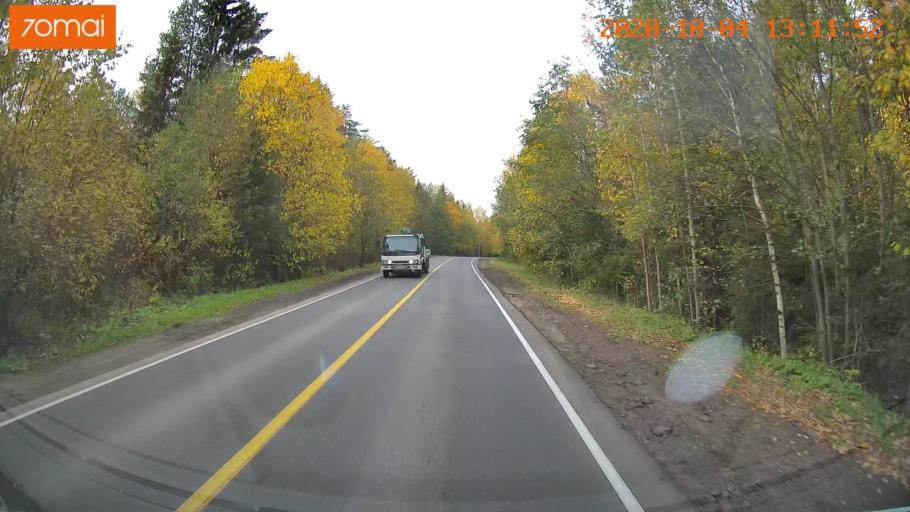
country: RU
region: Ivanovo
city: Bogorodskoye
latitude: 57.0796
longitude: 40.9365
